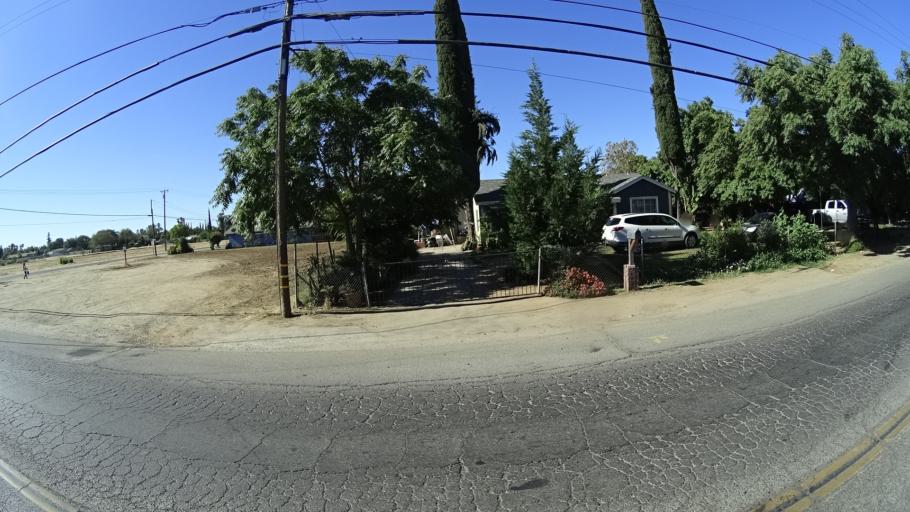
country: US
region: California
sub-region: Fresno County
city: West Park
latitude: 36.7575
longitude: -119.8361
